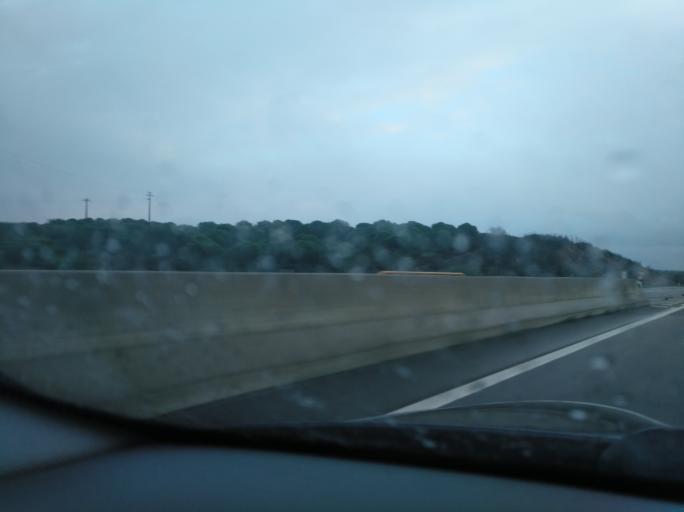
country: PT
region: Faro
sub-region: Castro Marim
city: Castro Marim
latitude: 37.2898
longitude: -7.4867
